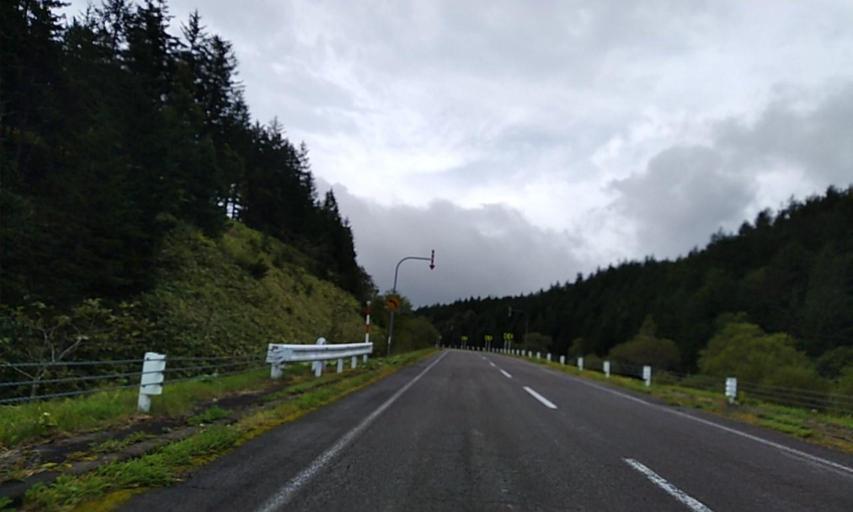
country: JP
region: Hokkaido
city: Abashiri
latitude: 43.6210
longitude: 144.5806
